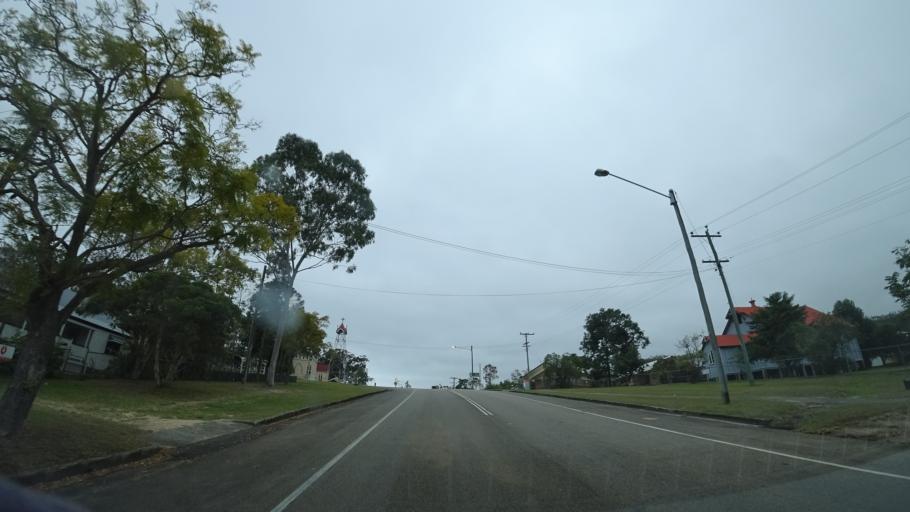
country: AU
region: Queensland
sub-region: Tablelands
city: Atherton
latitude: -17.3805
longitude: 145.3841
